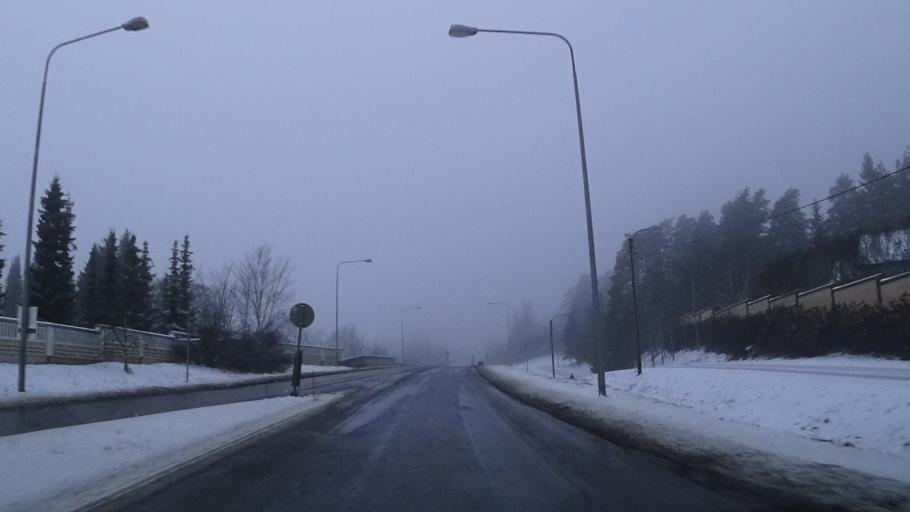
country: FI
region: Paijanne Tavastia
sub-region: Lahti
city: Hollola
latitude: 60.9811
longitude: 25.5461
